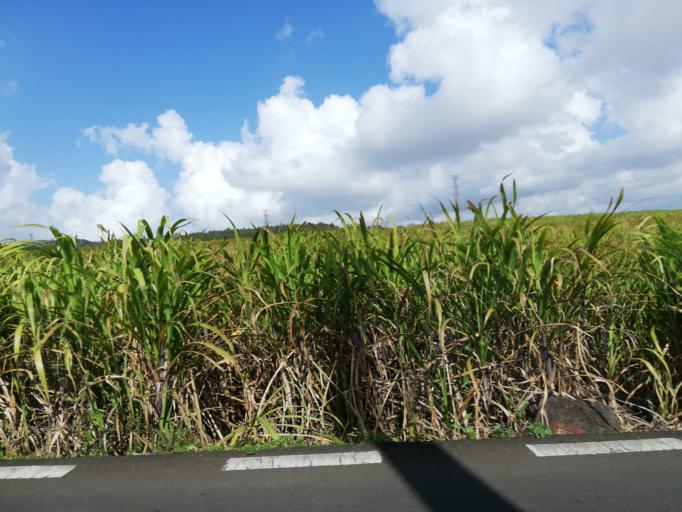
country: MU
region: Pamplemousses
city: Creve Coeur
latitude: -20.2045
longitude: 57.5695
